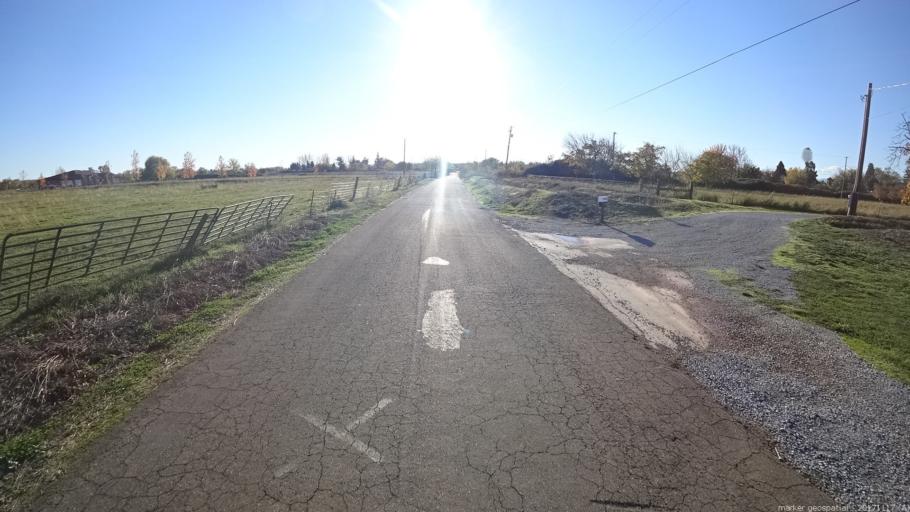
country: US
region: California
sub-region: Shasta County
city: Cottonwood
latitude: 40.4228
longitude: -122.2295
